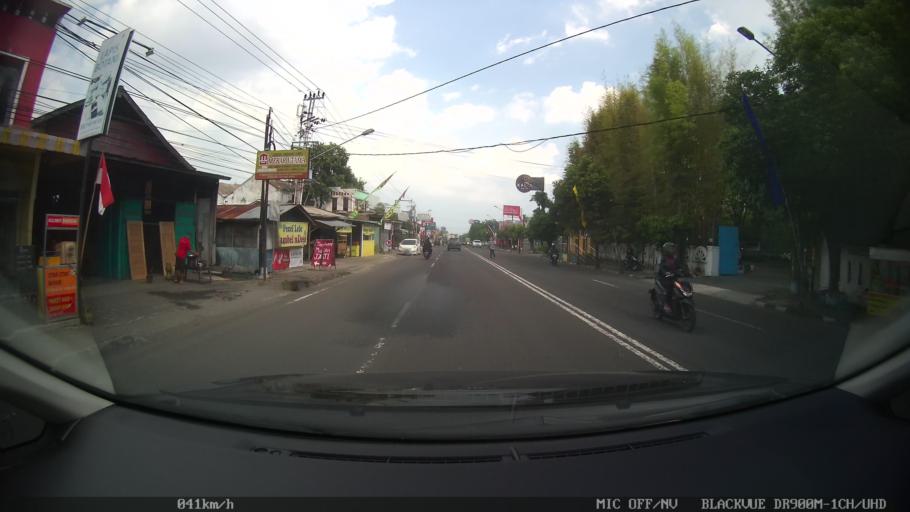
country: ID
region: Daerah Istimewa Yogyakarta
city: Yogyakarta
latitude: -7.8129
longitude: 110.4021
